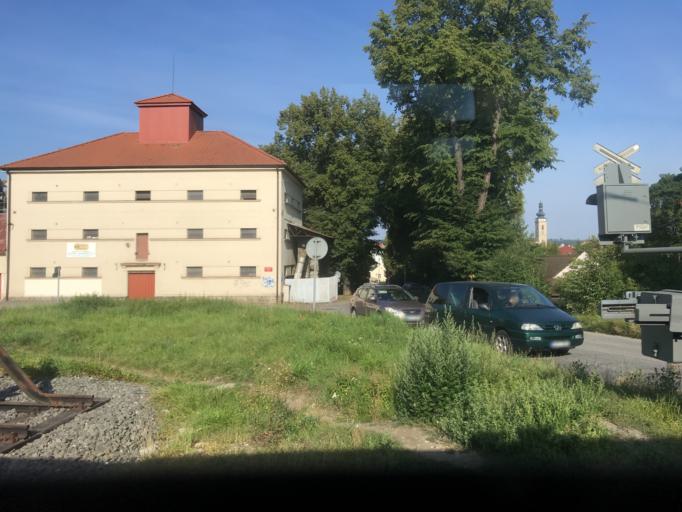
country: CZ
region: Jihocesky
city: Sobeslav
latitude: 49.2572
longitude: 14.7263
